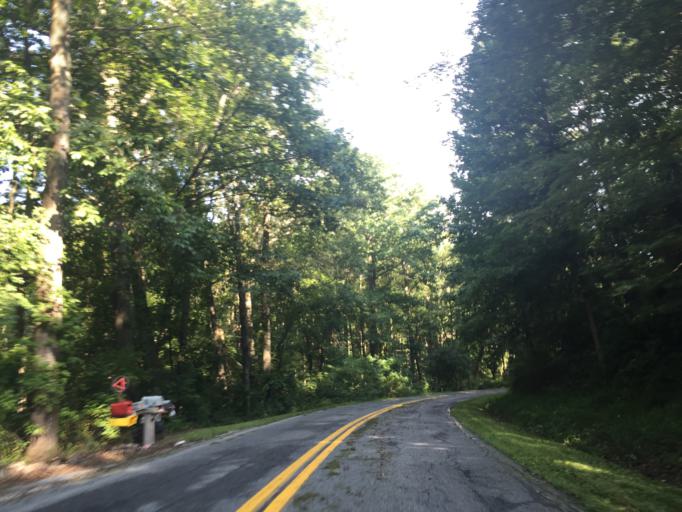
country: US
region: Maryland
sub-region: Carroll County
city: Manchester
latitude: 39.6352
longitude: -76.9036
